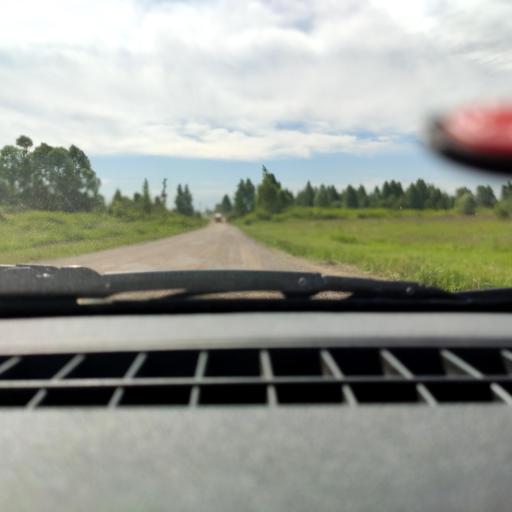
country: RU
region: Bashkortostan
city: Kabakovo
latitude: 54.7331
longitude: 56.2001
